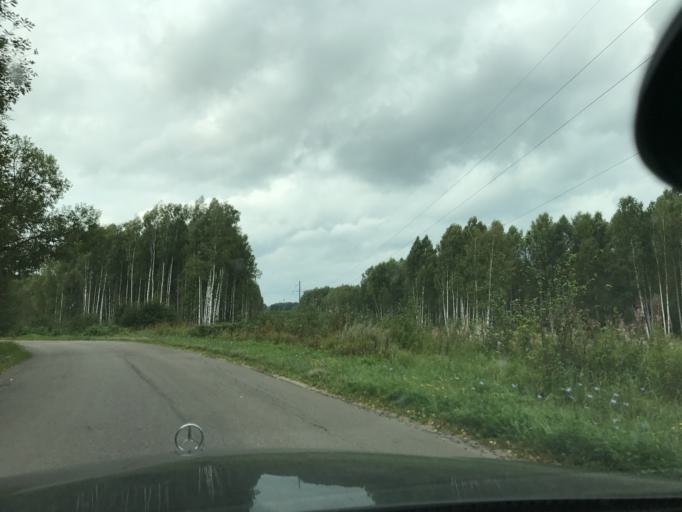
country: RU
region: Vladimir
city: Galitsy
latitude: 55.9965
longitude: 42.8254
